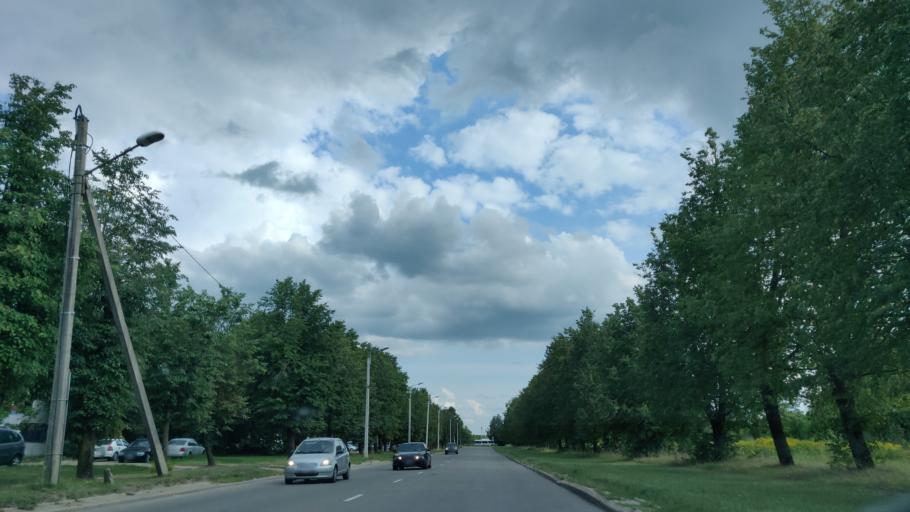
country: LT
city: Baltoji Voke
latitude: 54.6227
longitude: 25.1421
